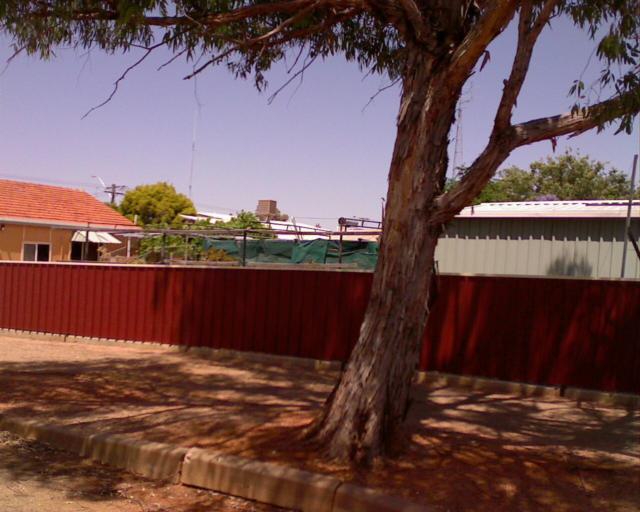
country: AU
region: Western Australia
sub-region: Merredin
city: Merredin
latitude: -30.9163
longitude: 118.2064
